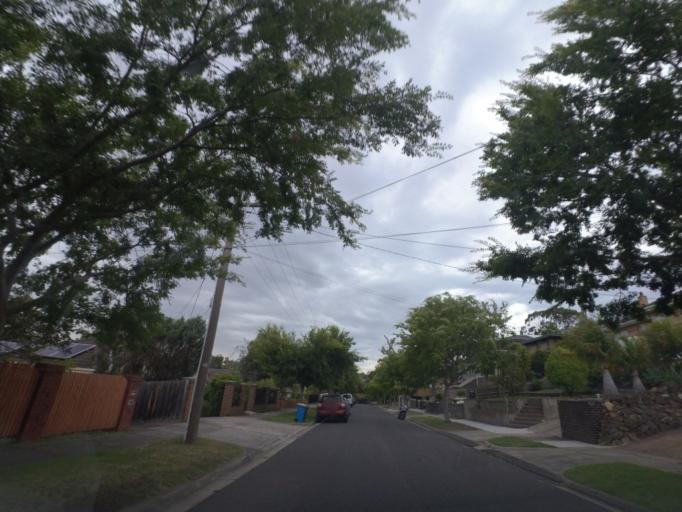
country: AU
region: Victoria
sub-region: Boroondara
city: Balwyn North
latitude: -37.7894
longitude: 145.0948
